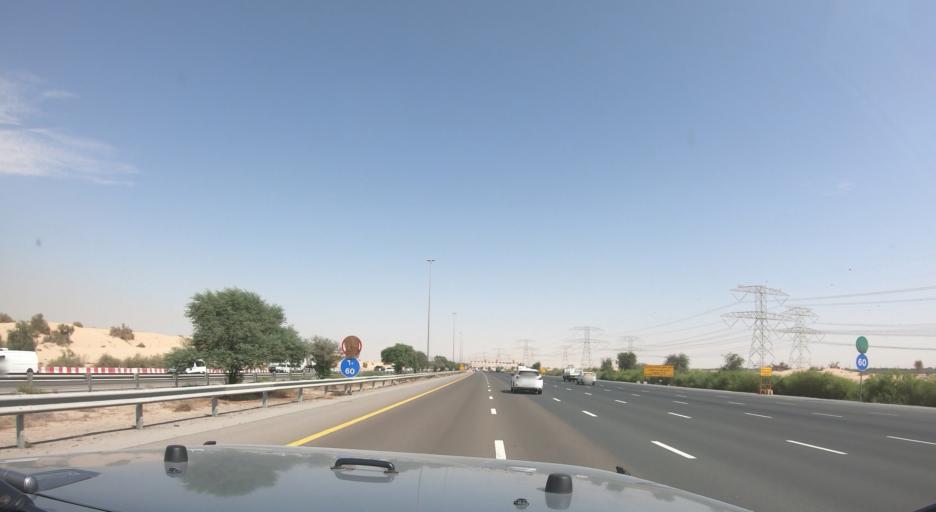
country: AE
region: Ash Shariqah
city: Sharjah
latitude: 25.1709
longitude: 55.5053
